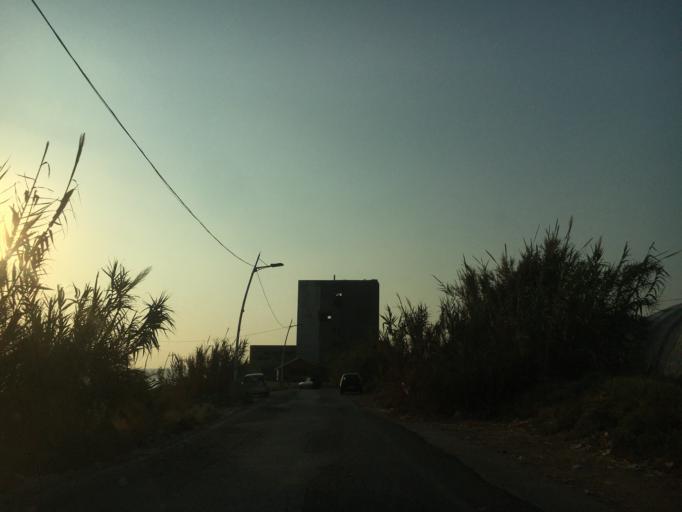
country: LB
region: Mont-Liban
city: Jbail
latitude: 34.1376
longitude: 35.6368
